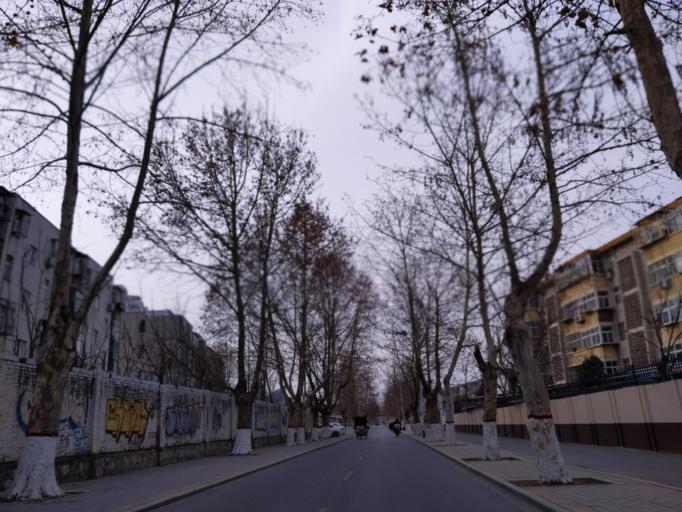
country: CN
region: Henan Sheng
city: Zhongyuanlu
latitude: 35.7596
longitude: 115.0444
